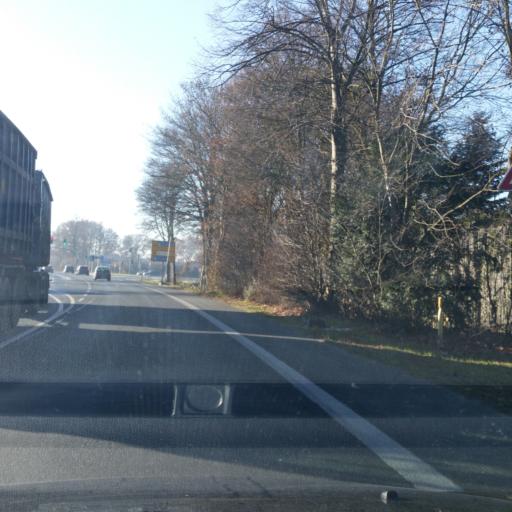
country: DE
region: North Rhine-Westphalia
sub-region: Regierungsbezirk Munster
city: Isselburg
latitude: 51.8195
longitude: 6.4437
